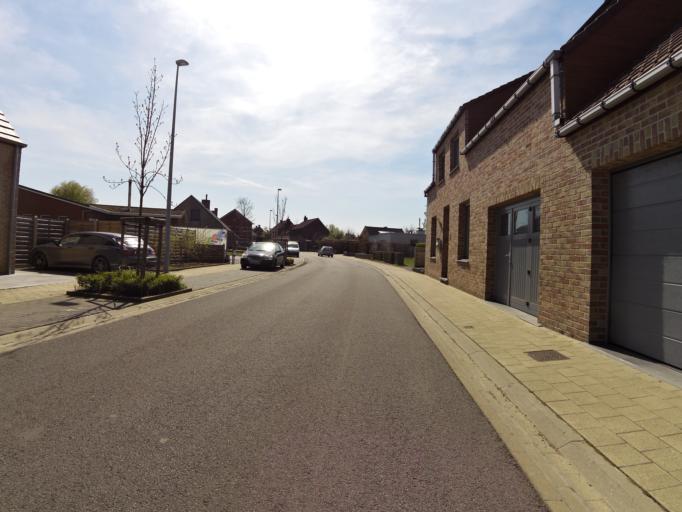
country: BE
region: Flanders
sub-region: Provincie West-Vlaanderen
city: Ichtegem
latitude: 51.0963
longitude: 3.0133
